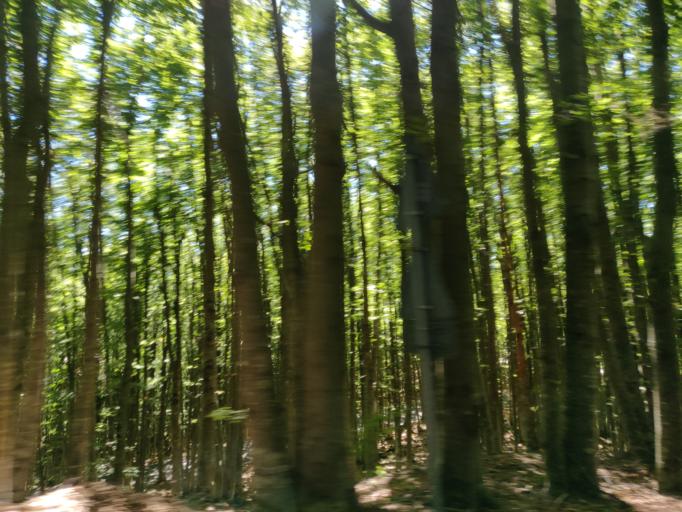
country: IT
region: Tuscany
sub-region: Provincia di Siena
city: Abbadia San Salvatore
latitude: 42.8837
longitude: 11.6228
